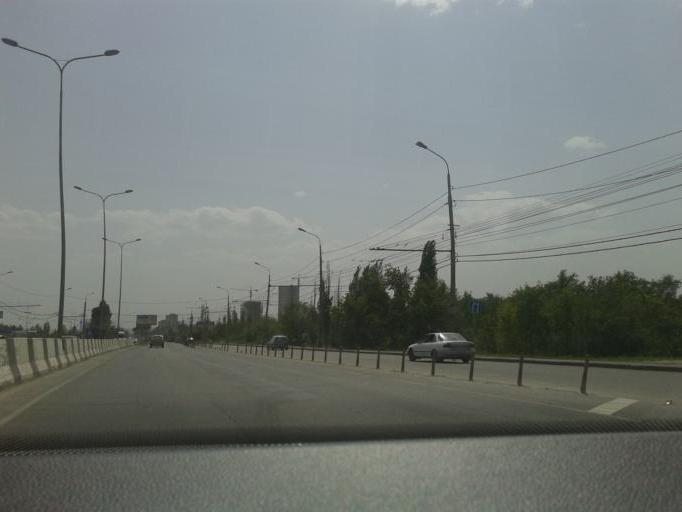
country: RU
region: Volgograd
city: Volgograd
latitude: 48.6346
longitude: 44.4294
